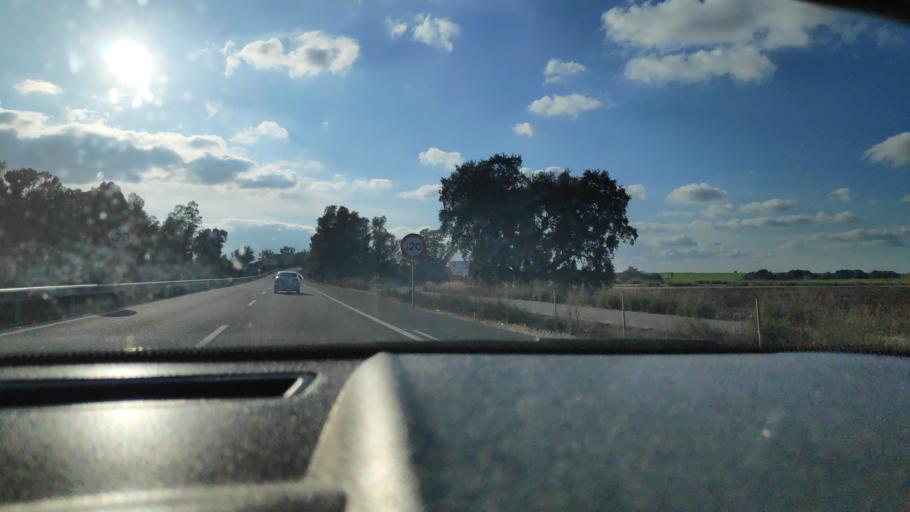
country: ES
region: Andalusia
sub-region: Provincia de Sevilla
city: La Luisiana
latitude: 37.5207
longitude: -5.3125
